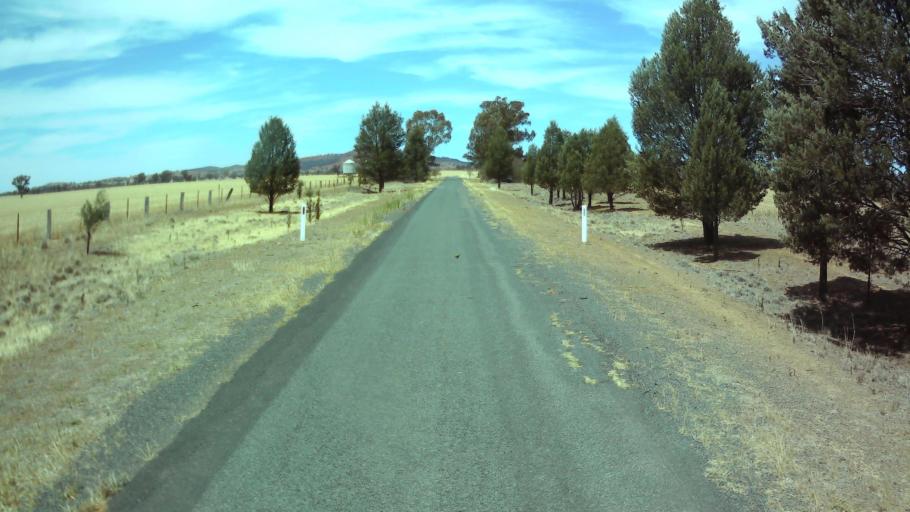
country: AU
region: New South Wales
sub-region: Weddin
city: Grenfell
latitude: -33.7568
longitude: 148.0937
